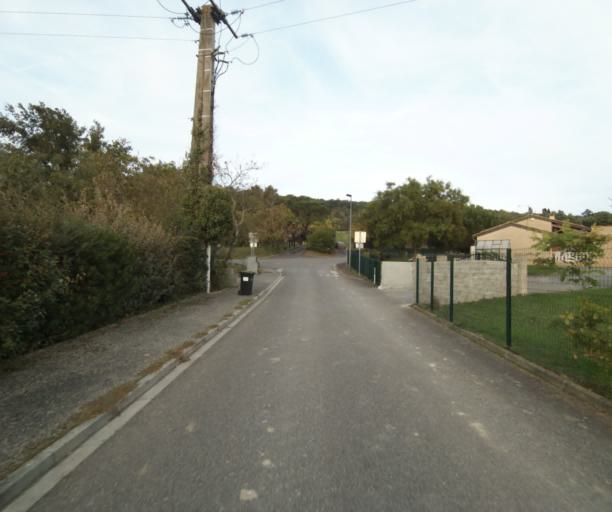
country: FR
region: Midi-Pyrenees
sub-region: Departement du Tarn-et-Garonne
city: Pompignan
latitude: 43.8210
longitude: 1.3089
